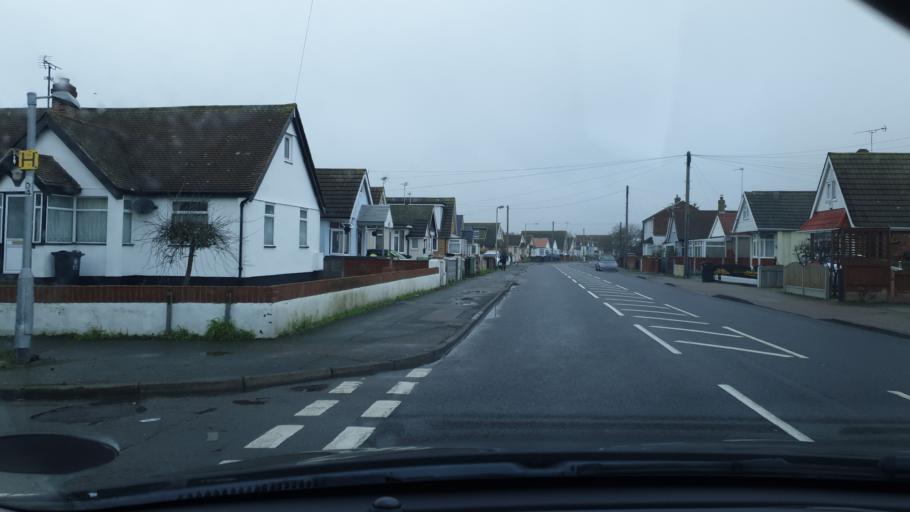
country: GB
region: England
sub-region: Essex
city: Clacton-on-Sea
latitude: 51.7789
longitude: 1.1209
